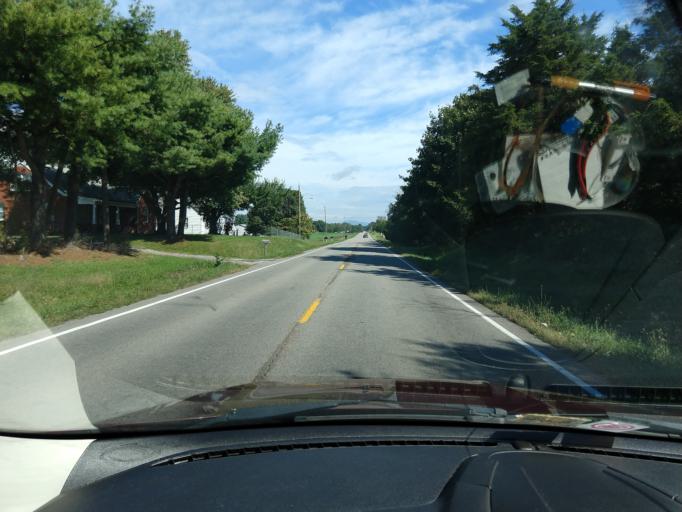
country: US
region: Virginia
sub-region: Augusta County
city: Crimora
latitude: 38.1923
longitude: -78.8390
